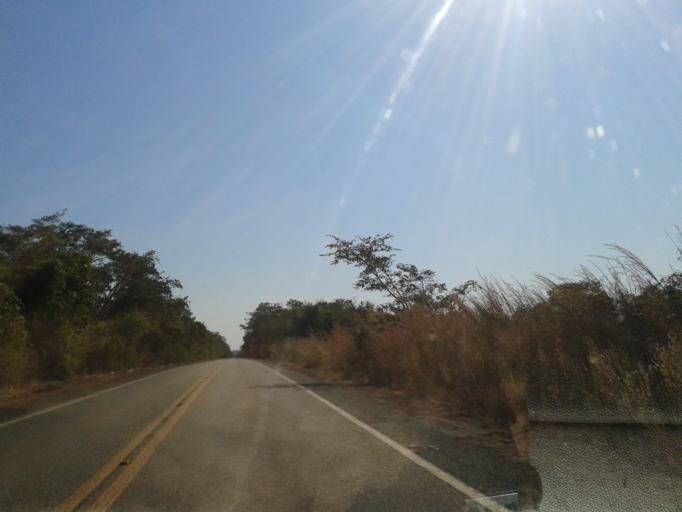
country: BR
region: Goias
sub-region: Mozarlandia
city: Mozarlandia
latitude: -14.6799
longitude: -50.5382
